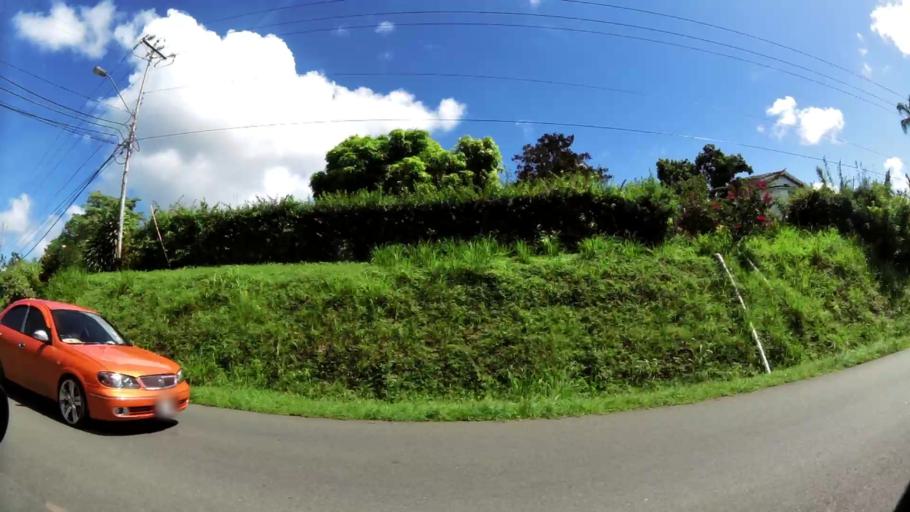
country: TT
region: Tobago
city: Scarborough
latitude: 11.1963
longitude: -60.7947
